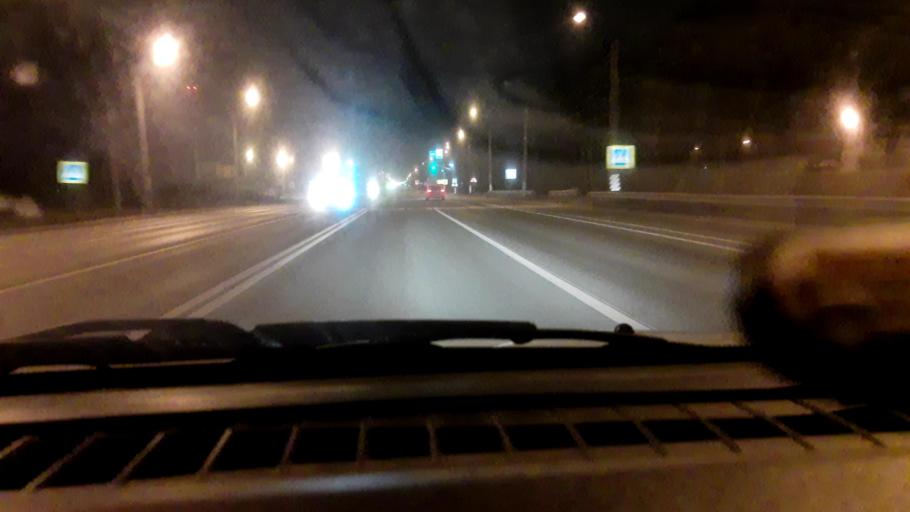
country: RU
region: Nizjnij Novgorod
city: Gorbatovka
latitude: 56.3085
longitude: 43.7395
